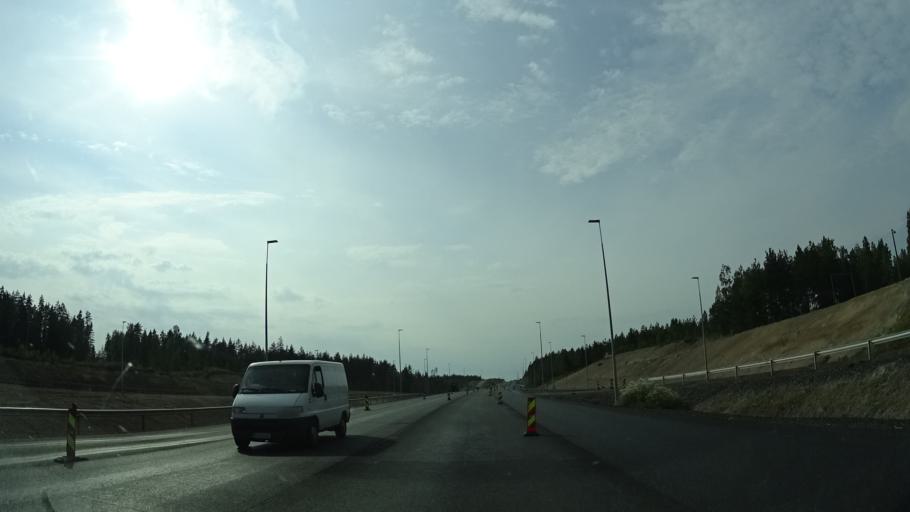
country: FI
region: South Karelia
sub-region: Lappeenranta
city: Luumaeki
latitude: 60.9286
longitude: 27.6271
